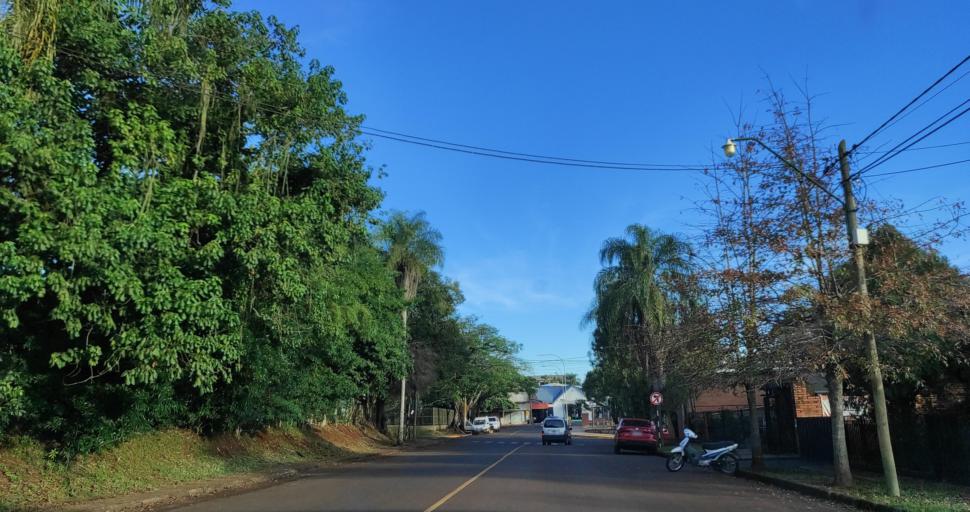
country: AR
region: Misiones
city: Puerto Rico
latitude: -26.8015
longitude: -55.0205
